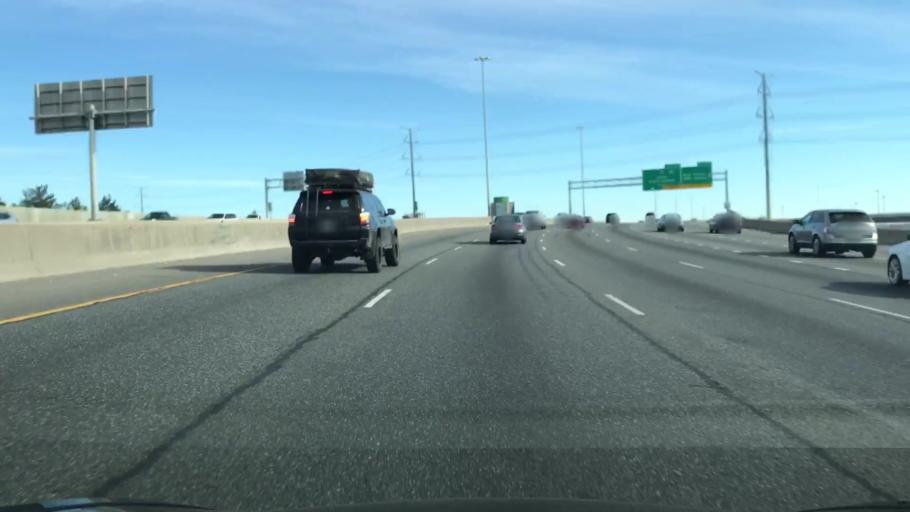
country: US
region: Colorado
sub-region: Denver County
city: Denver
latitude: 39.7662
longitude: -105.0002
